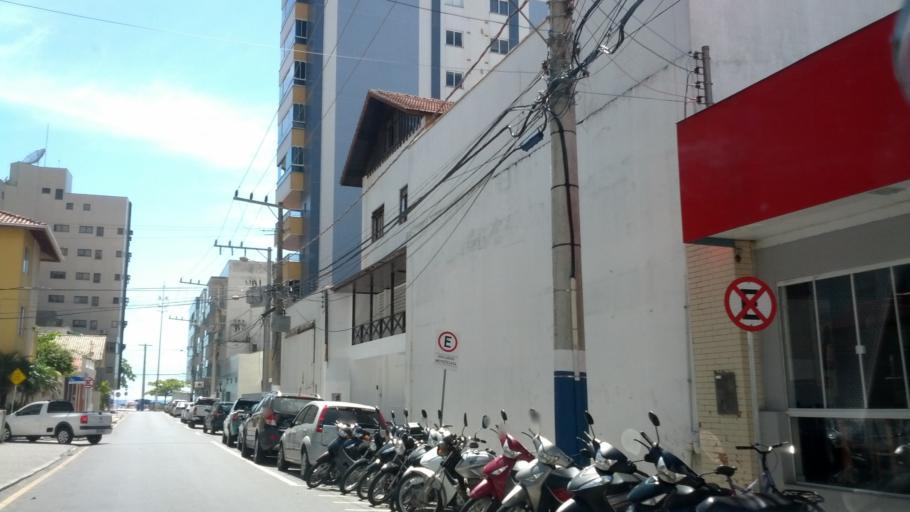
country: BR
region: Santa Catarina
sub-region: Balneario Camboriu
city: Balneario Camboriu
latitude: -26.9983
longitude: -48.6258
